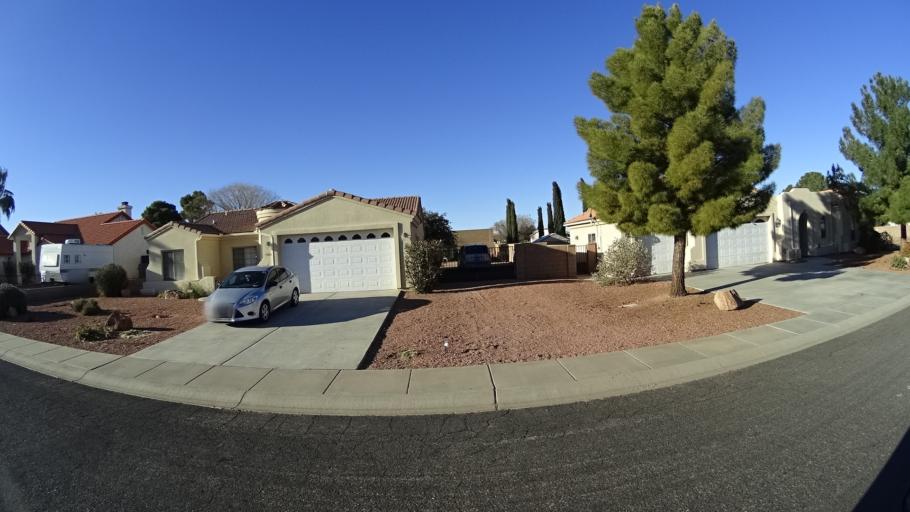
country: US
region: Arizona
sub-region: Mohave County
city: New Kingman-Butler
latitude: 35.2221
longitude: -113.9724
